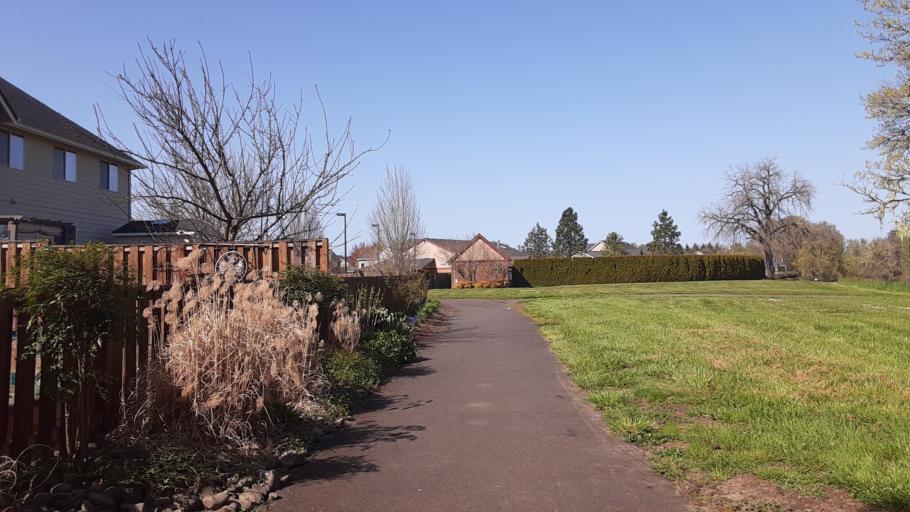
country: US
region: Oregon
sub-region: Benton County
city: Corvallis
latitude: 44.5286
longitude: -123.2556
